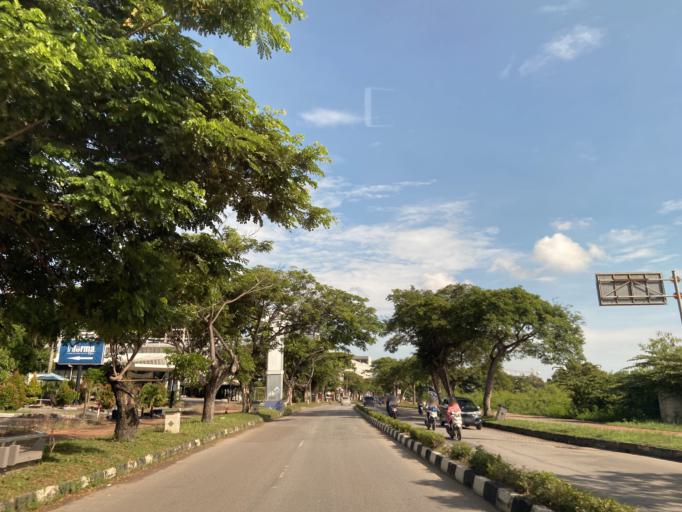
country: SG
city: Singapore
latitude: 1.1290
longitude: 104.0485
